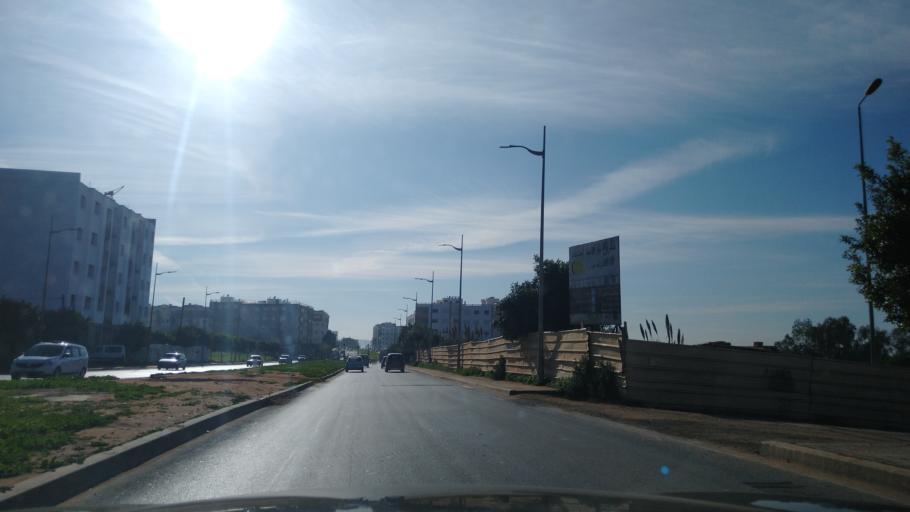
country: MA
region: Rabat-Sale-Zemmour-Zaer
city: Sale
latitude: 34.0081
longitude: -6.7416
